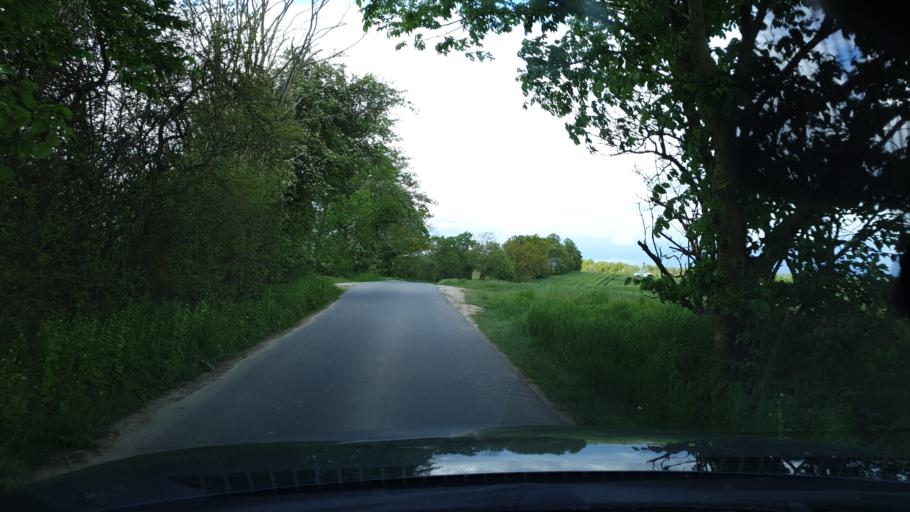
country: DE
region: Mecklenburg-Vorpommern
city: Bernitt
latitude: 53.9260
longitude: 11.8398
